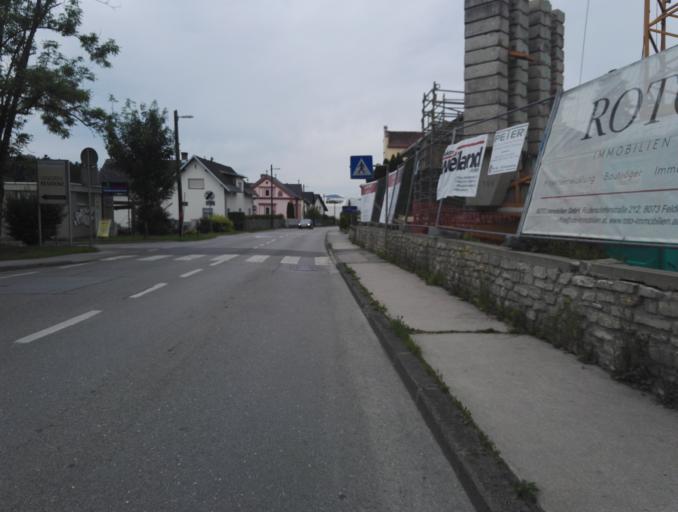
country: AT
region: Styria
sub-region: Graz Stadt
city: Mariatrost
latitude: 47.0788
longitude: 15.4800
